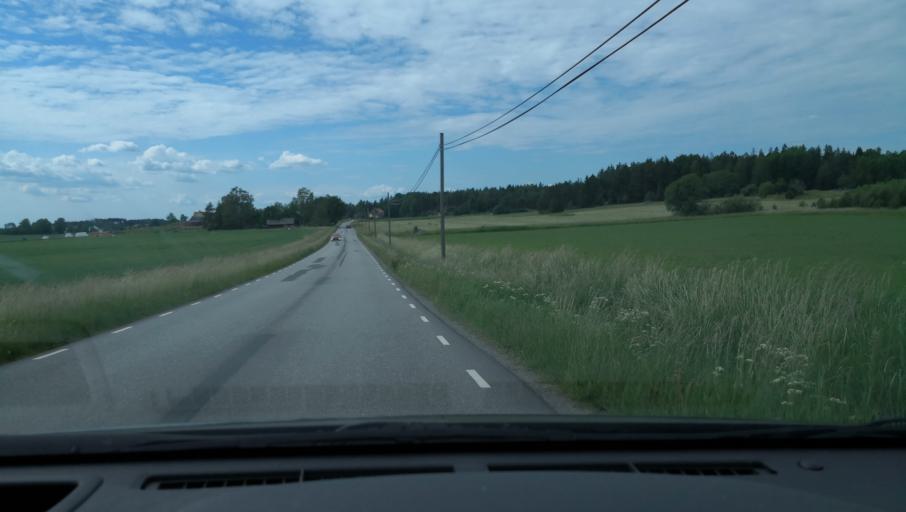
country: SE
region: Uppsala
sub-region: Uppsala Kommun
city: Uppsala
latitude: 59.8065
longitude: 17.5292
